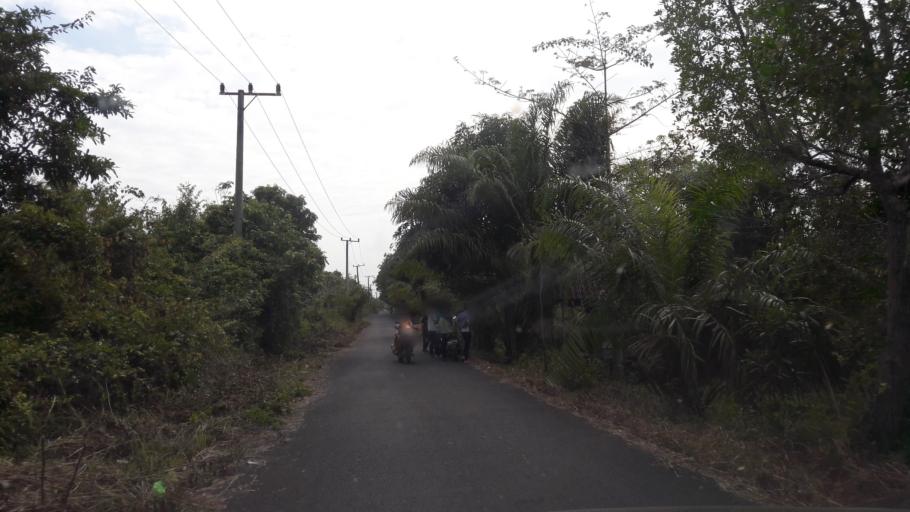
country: ID
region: South Sumatra
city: Gunungmenang
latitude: -3.0984
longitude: 104.0480
